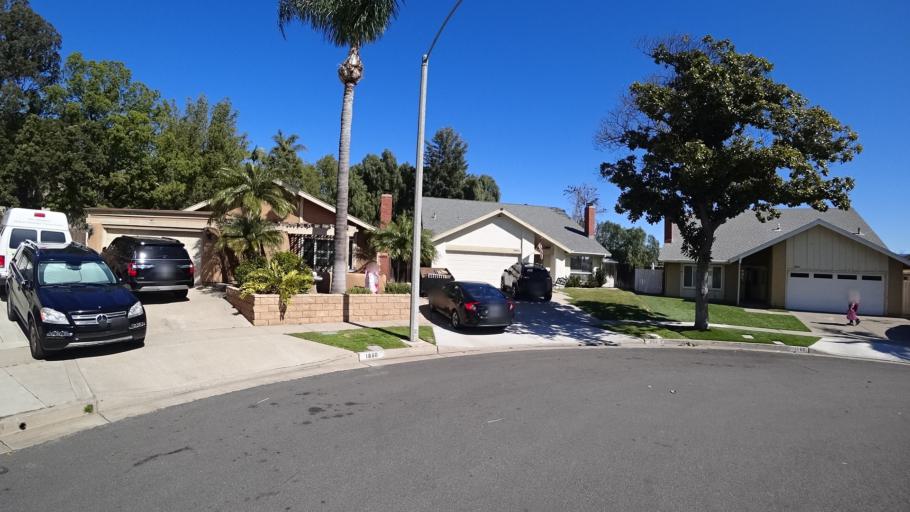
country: US
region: California
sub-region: Orange County
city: Yorba Linda
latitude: 33.8715
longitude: -117.8065
